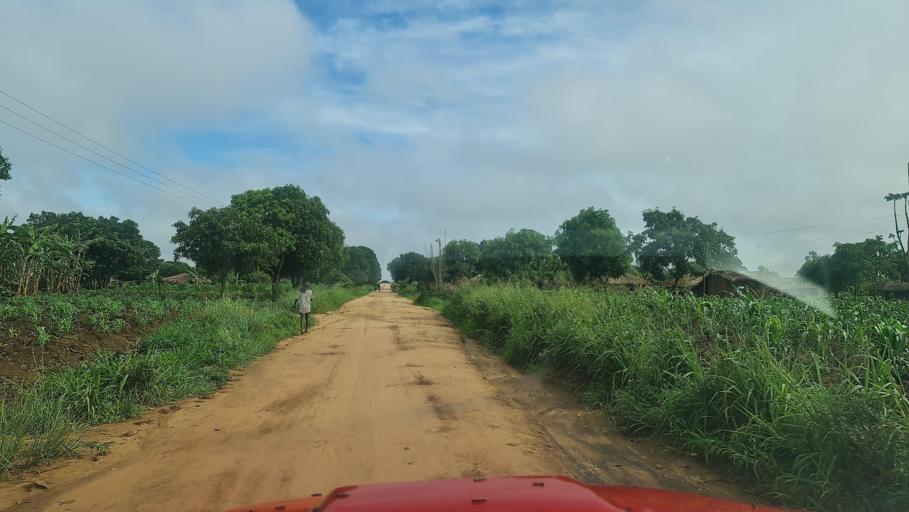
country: MW
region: Southern Region
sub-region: Nsanje District
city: Nsanje
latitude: -17.3037
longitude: 35.5934
